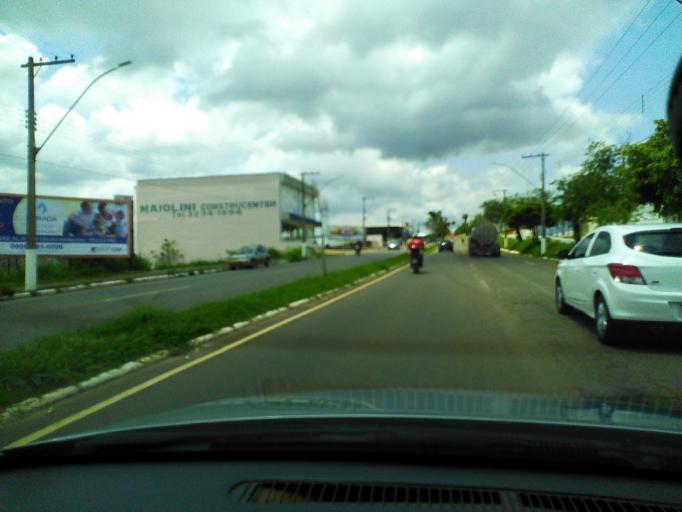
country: BR
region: Minas Gerais
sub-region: Tres Coracoes
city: Tres Coracoes
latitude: -21.6818
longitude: -45.2659
